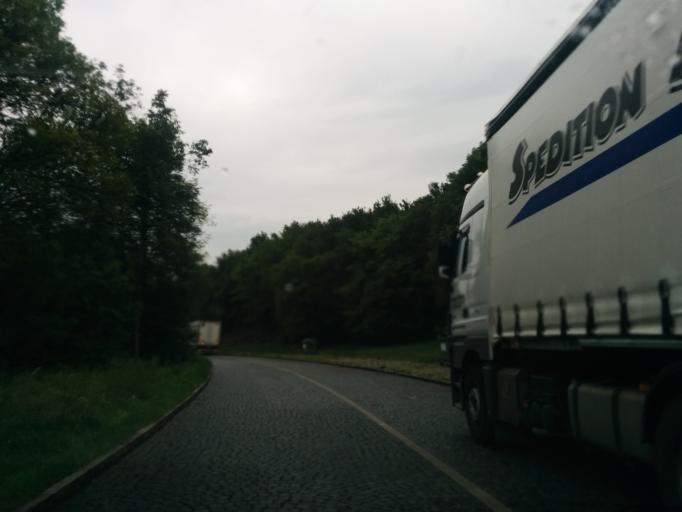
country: DE
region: Bavaria
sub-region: Regierungsbezirk Unterfranken
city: Estenfeld
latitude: 49.8632
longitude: 9.9937
